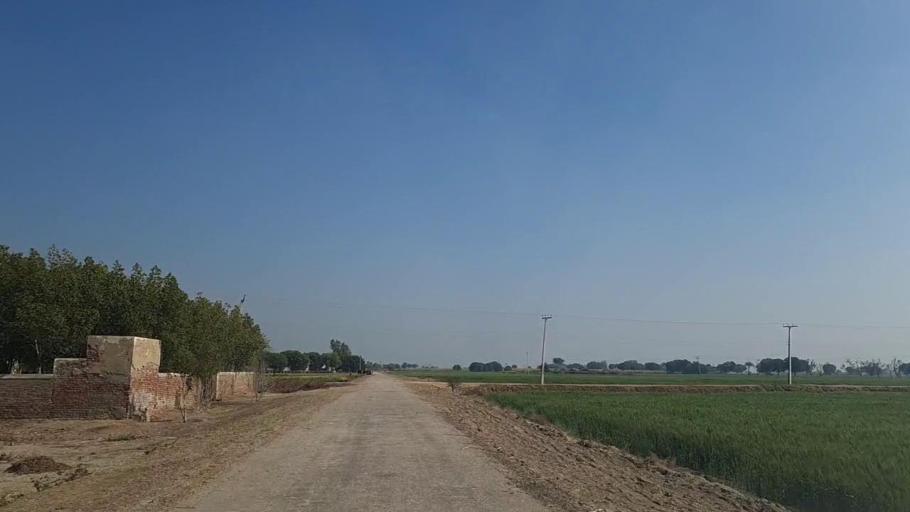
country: PK
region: Sindh
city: Shahpur Chakar
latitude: 26.2027
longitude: 68.5730
